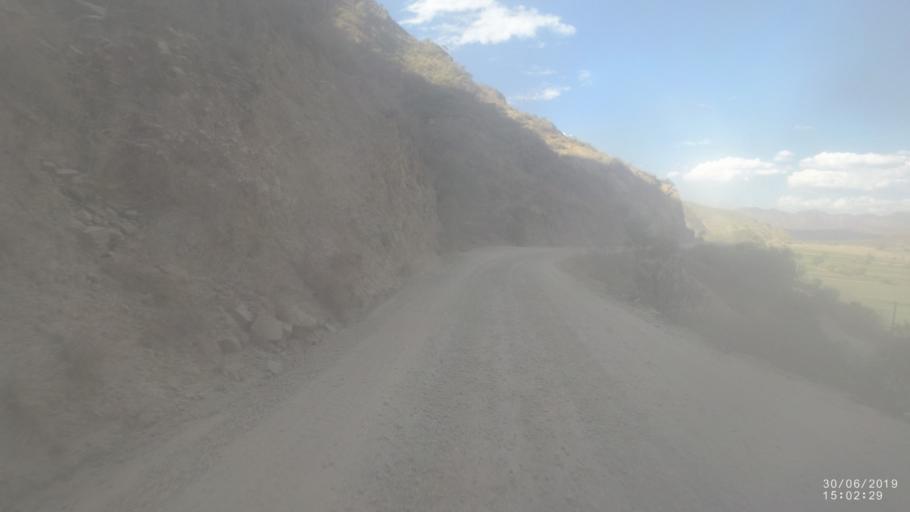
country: BO
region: Cochabamba
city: Irpa Irpa
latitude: -17.7321
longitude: -66.3322
